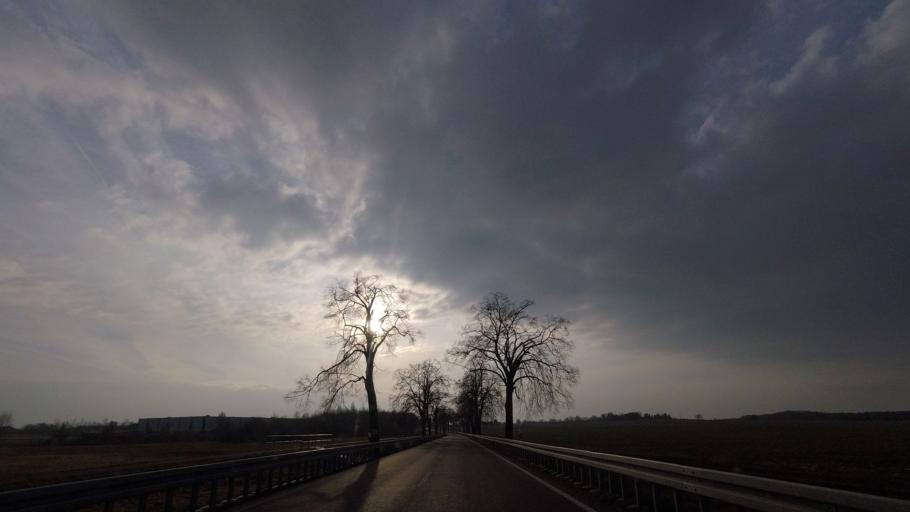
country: DE
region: Brandenburg
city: Wiesenburg
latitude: 52.1209
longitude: 12.4733
